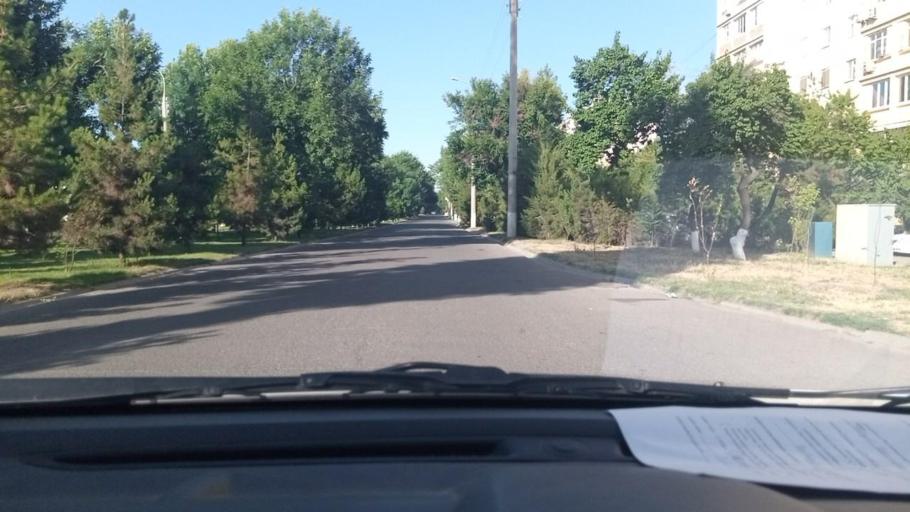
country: UZ
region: Toshkent
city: Salor
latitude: 41.3207
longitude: 69.3608
